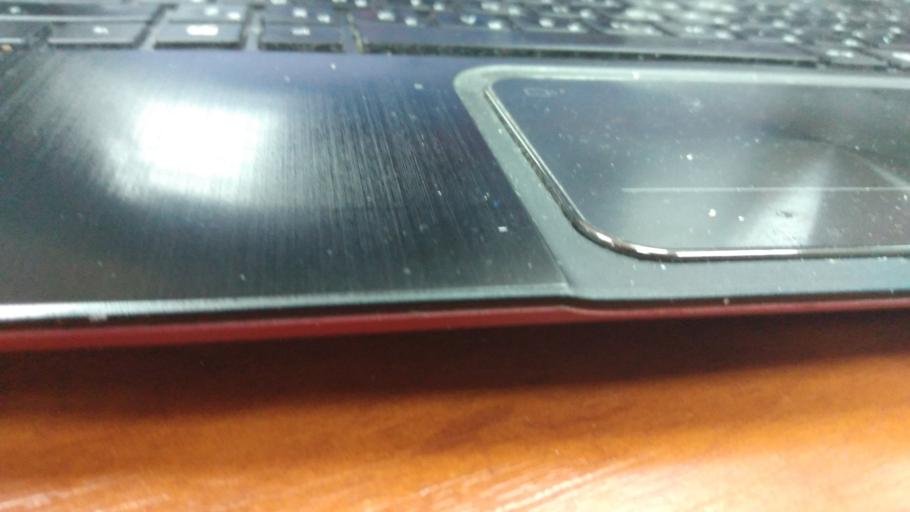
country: RU
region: Moskovskaya
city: Mamontovka
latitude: 55.9854
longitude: 37.8104
